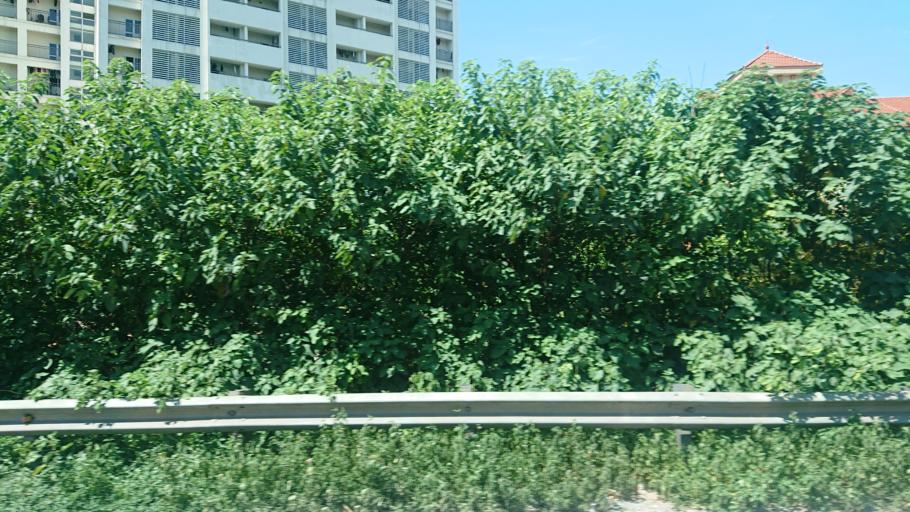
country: VN
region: Ha Noi
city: Van Dien
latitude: 20.9608
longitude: 105.8482
